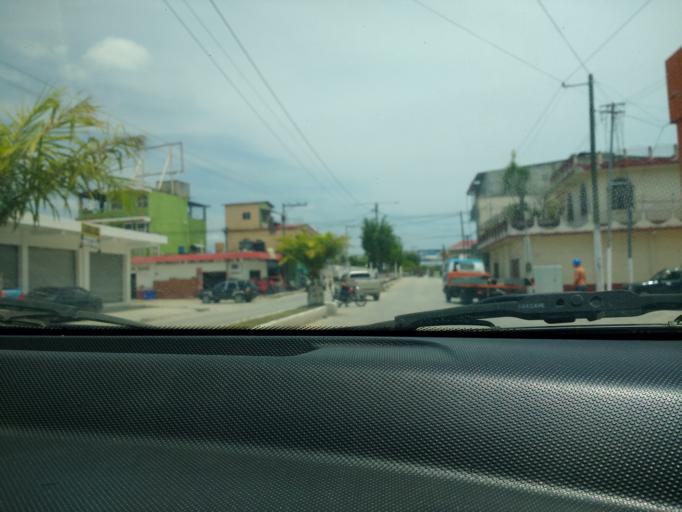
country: GT
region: Peten
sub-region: Municipio de Flores
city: Flores
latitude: 16.9181
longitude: -89.9074
